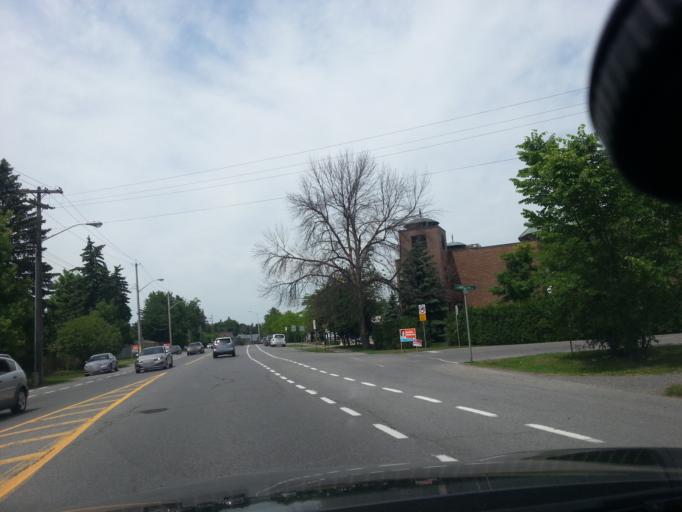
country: CA
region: Ontario
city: Ottawa
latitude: 45.3706
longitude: -75.7045
